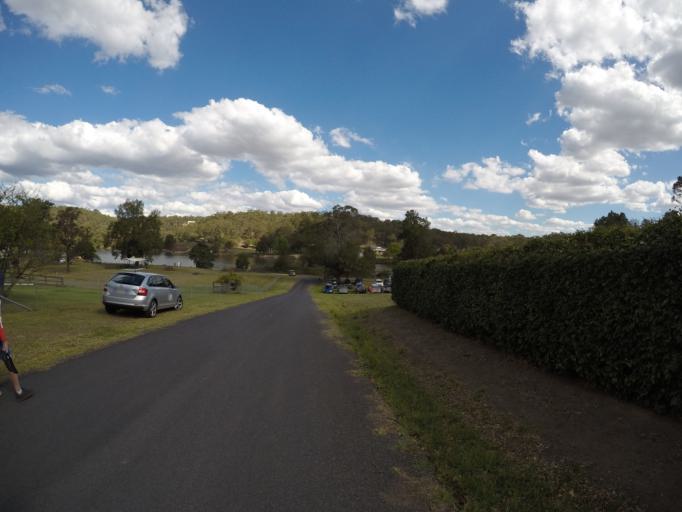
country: AU
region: New South Wales
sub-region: Hawkesbury
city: Pitt Town
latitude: -33.4716
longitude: 150.8907
